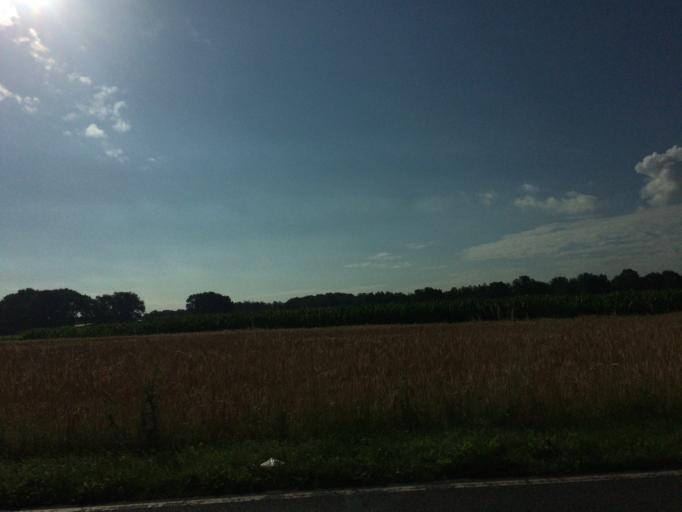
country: DE
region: North Rhine-Westphalia
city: Dorsten
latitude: 51.6788
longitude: 6.9857
